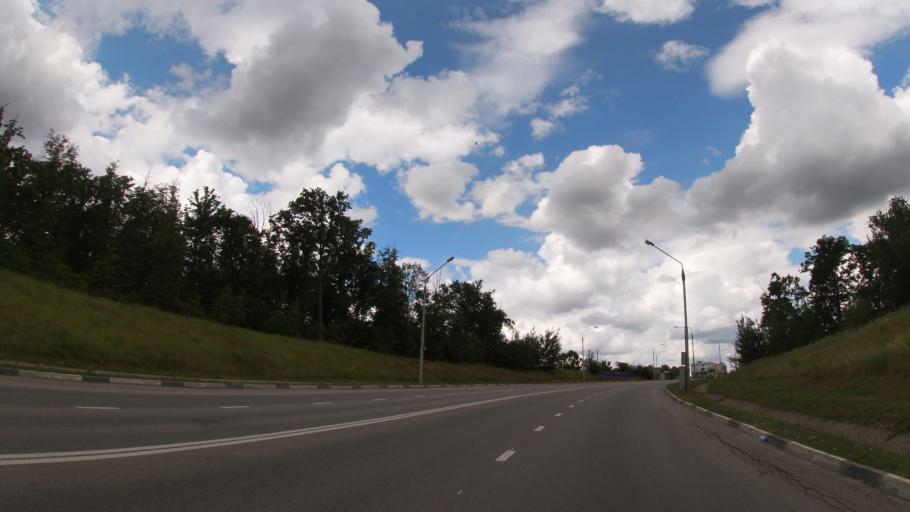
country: RU
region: Belgorod
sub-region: Belgorodskiy Rayon
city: Belgorod
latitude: 50.6240
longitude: 36.6115
